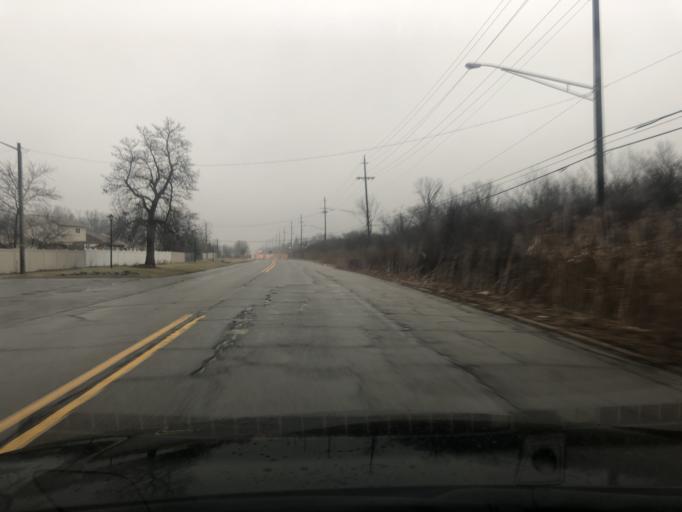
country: US
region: Michigan
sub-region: Wayne County
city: Gibraltar
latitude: 42.1019
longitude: -83.2249
